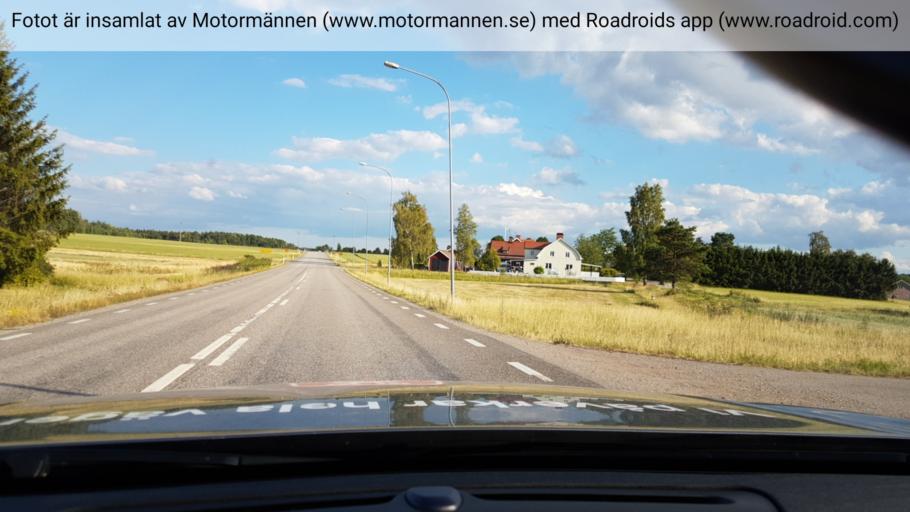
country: SE
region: Uppsala
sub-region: Heby Kommun
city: Heby
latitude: 59.9338
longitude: 16.8700
